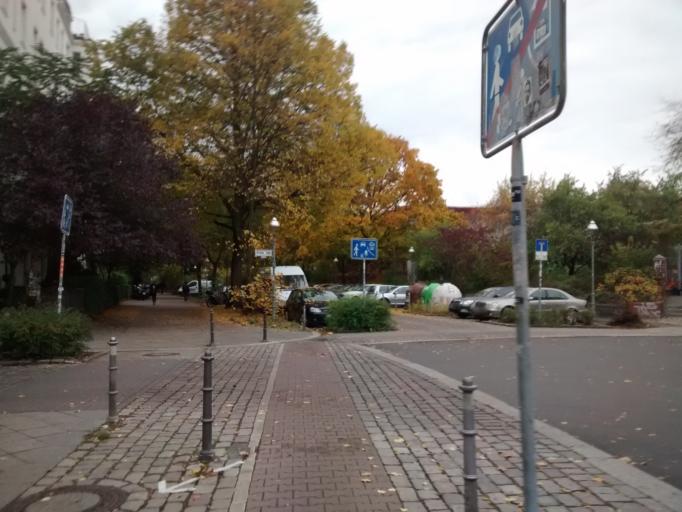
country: DE
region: Berlin
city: Moabit
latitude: 52.5327
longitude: 13.3394
